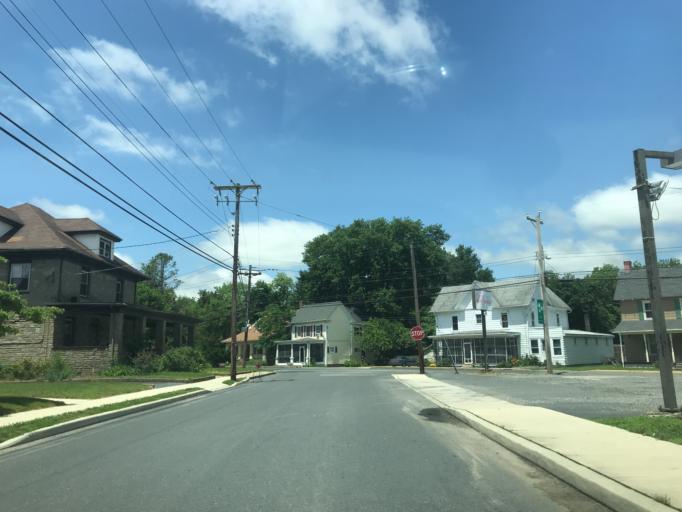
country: US
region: Maryland
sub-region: Caroline County
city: Federalsburg
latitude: 38.6949
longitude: -75.7675
